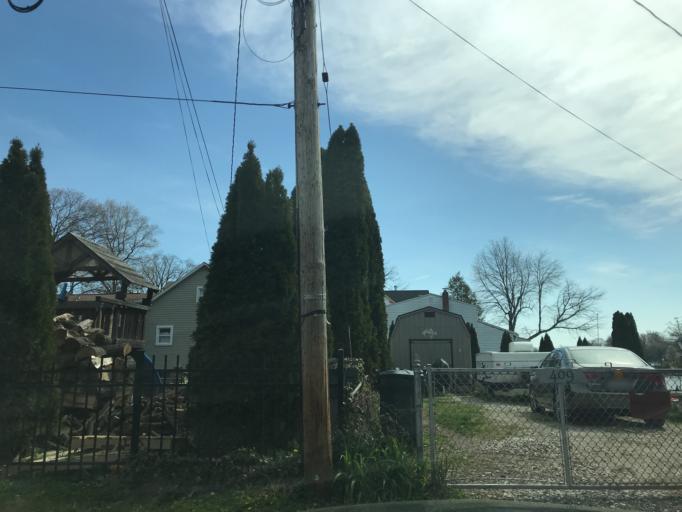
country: US
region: Maryland
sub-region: Baltimore County
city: Middle River
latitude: 39.3036
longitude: -76.4283
